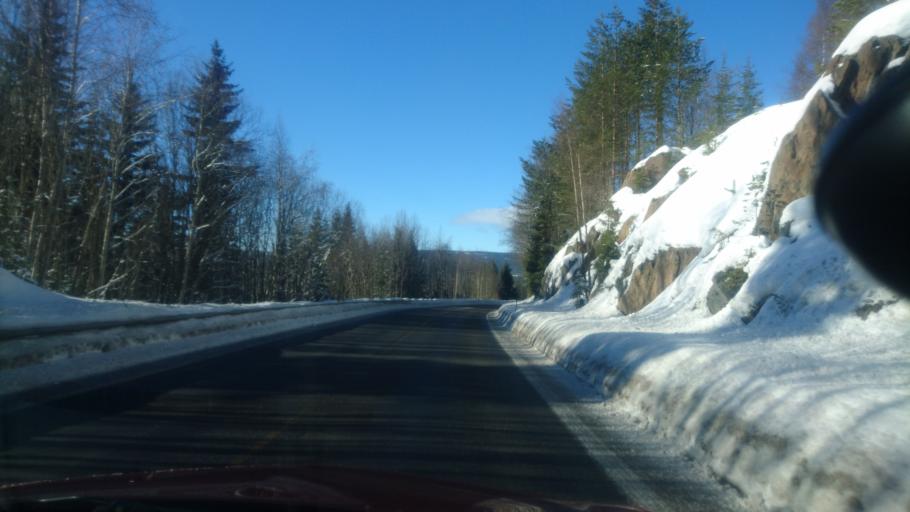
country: NO
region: Hedmark
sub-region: Trysil
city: Innbygda
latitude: 61.2623
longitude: 12.3404
